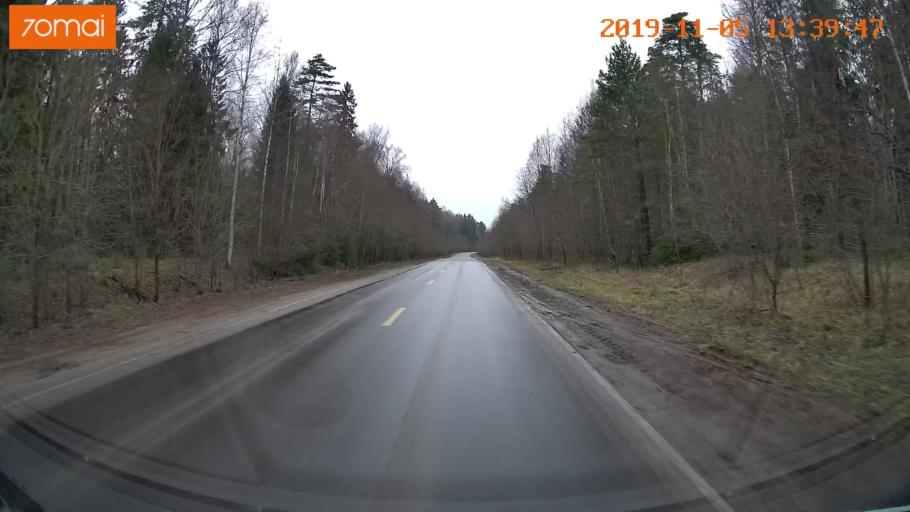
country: RU
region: Ivanovo
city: Shuya
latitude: 56.9431
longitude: 41.3845
